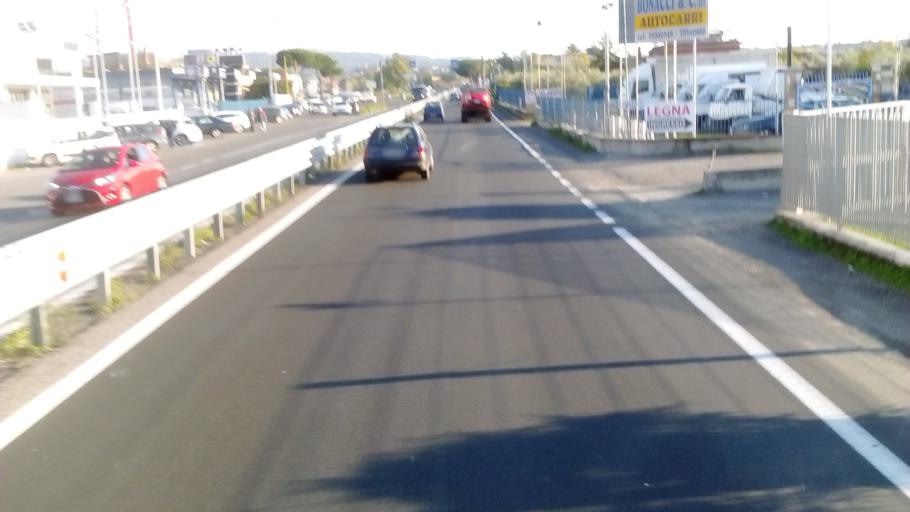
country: IT
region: Latium
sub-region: Citta metropolitana di Roma Capitale
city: Ciampino
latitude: 41.7835
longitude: 12.6006
